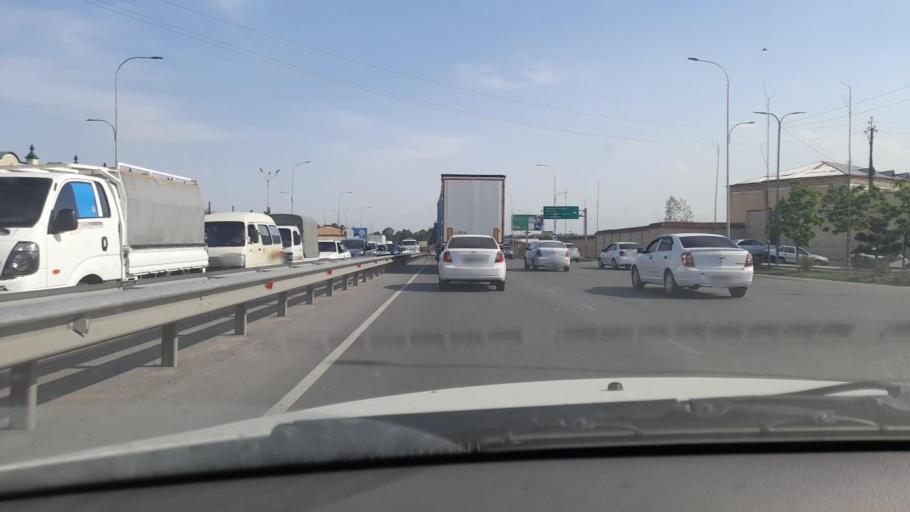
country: UZ
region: Samarqand
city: Samarqand
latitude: 39.6800
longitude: 67.0047
